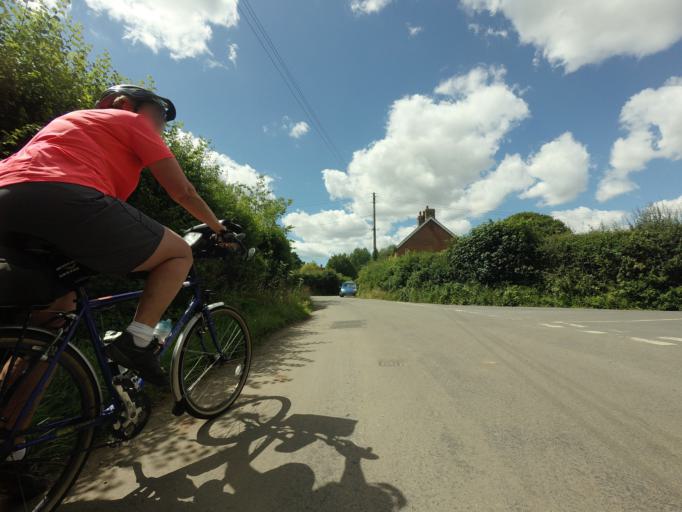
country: GB
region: England
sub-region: East Sussex
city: Hailsham
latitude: 50.8647
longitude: 0.1595
